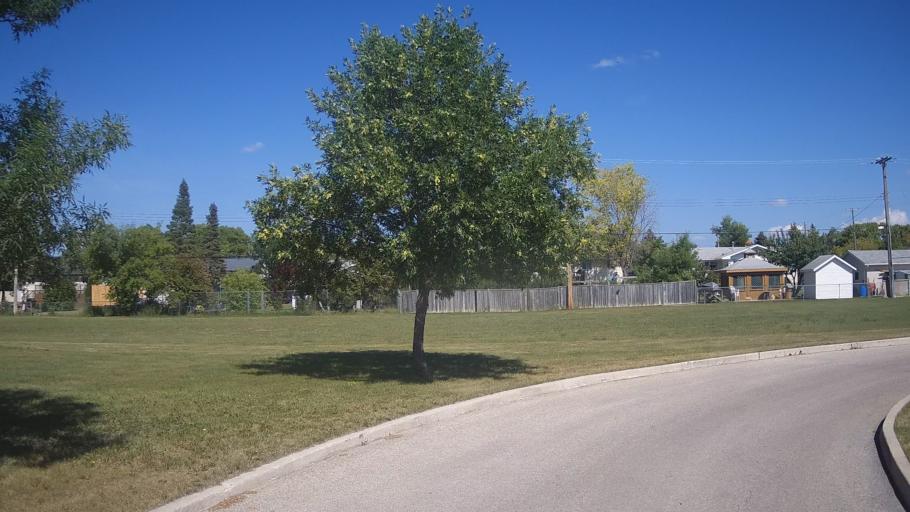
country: CA
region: Manitoba
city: Stonewall
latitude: 50.1307
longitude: -97.3348
